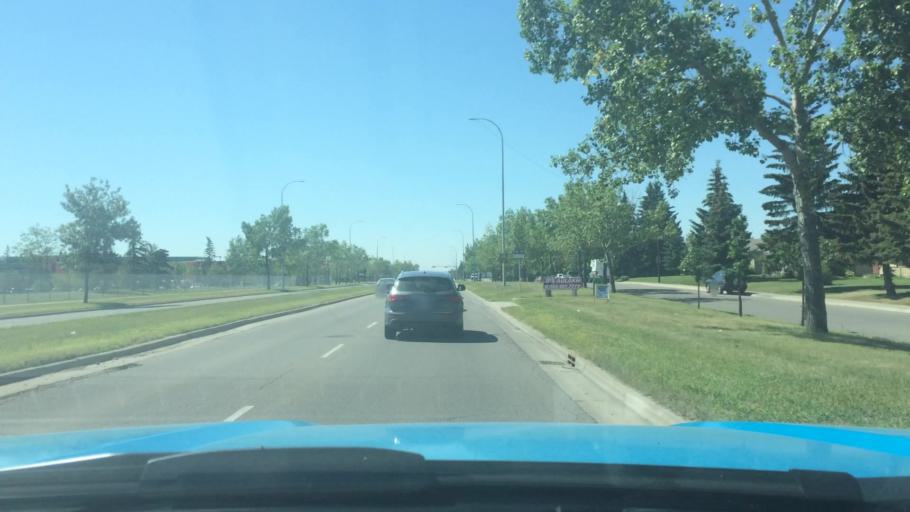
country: CA
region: Alberta
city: Calgary
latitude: 51.0794
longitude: -113.9585
